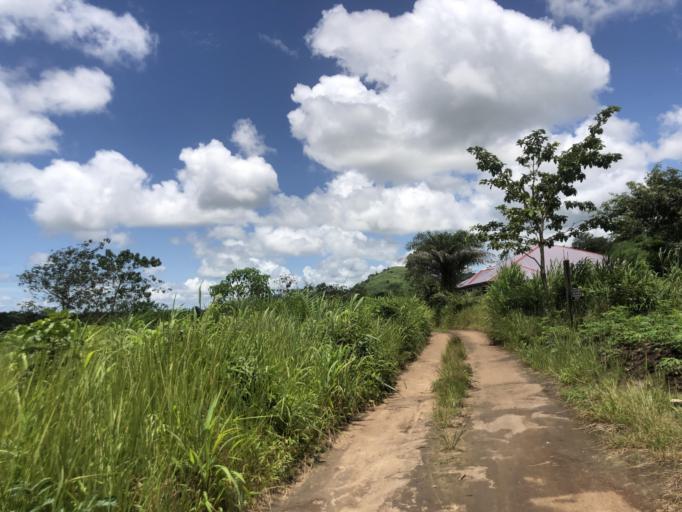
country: SL
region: Northern Province
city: Makeni
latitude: 8.8513
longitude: -12.0622
